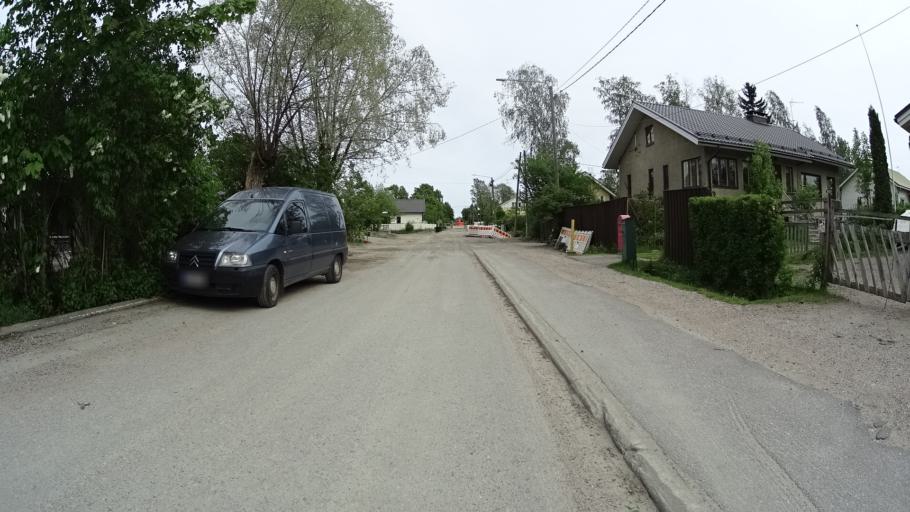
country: FI
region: Uusimaa
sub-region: Helsinki
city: Vantaa
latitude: 60.2984
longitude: 24.9997
